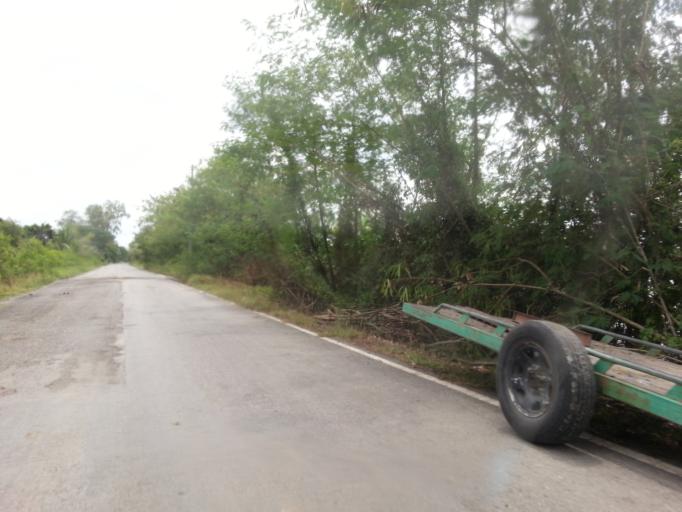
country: TH
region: Pathum Thani
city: Ban Lam Luk Ka
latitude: 14.0134
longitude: 100.8460
